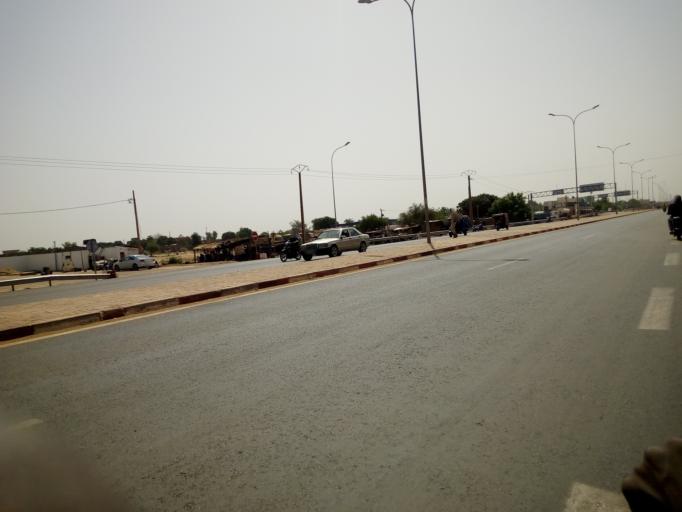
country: ML
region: Segou
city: Segou
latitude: 13.4367
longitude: -6.2368
